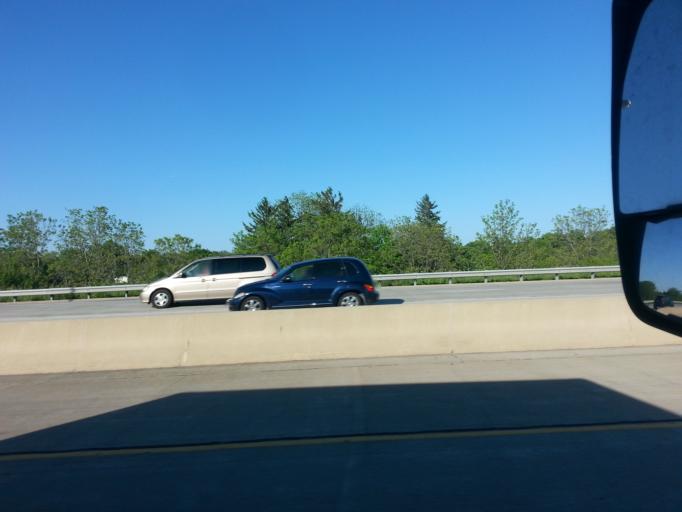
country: US
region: Illinois
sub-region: McLean County
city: Bloomington
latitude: 40.4560
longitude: -89.0260
